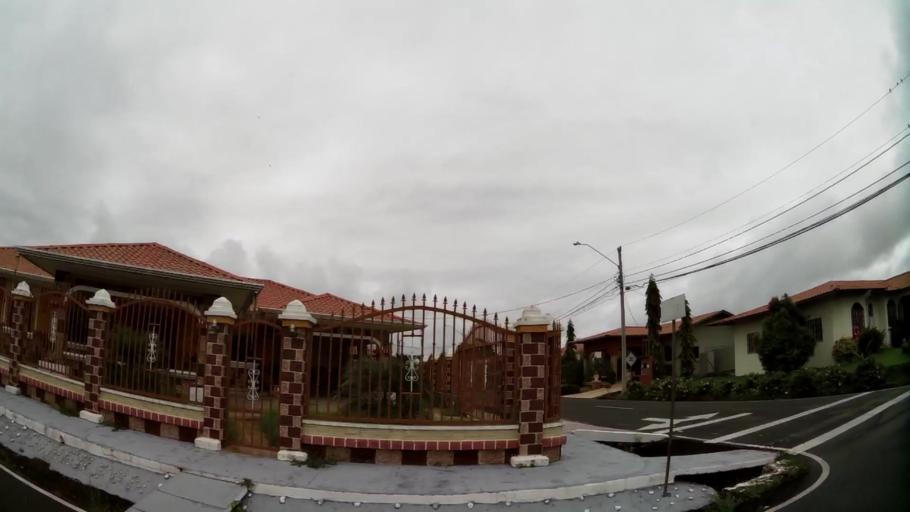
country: PA
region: Chiriqui
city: David
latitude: 8.4355
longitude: -82.4431
